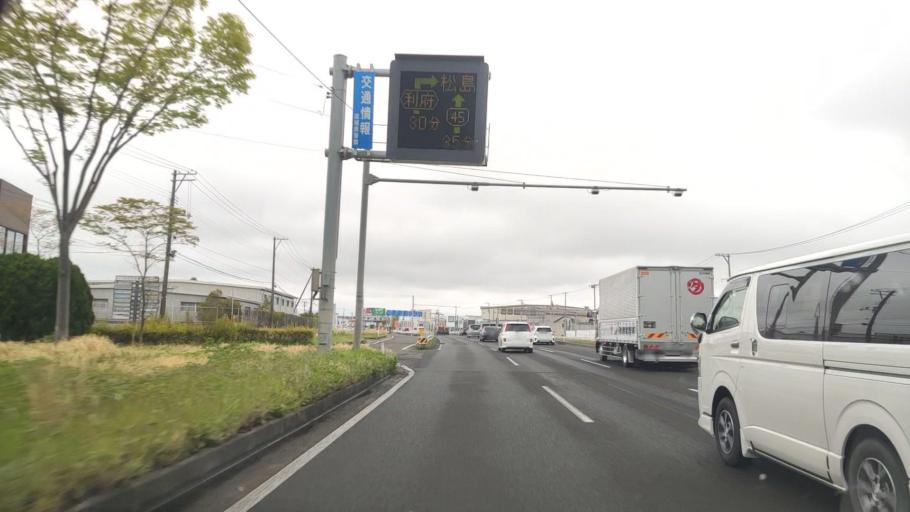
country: JP
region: Miyagi
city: Sendai-shi
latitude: 38.2572
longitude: 140.9360
